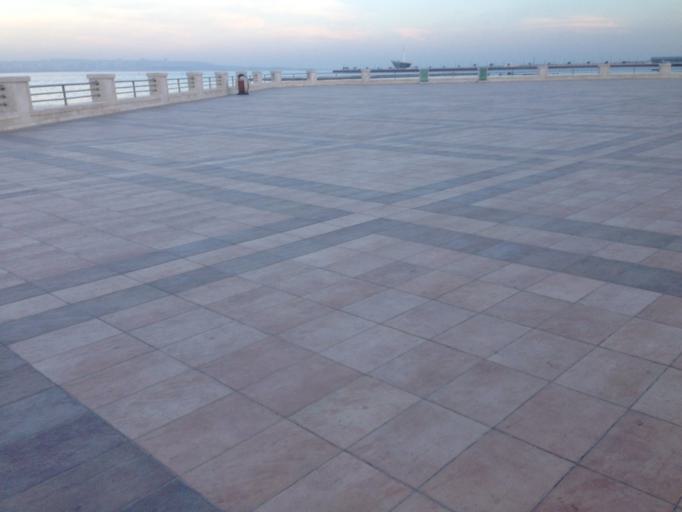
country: AZ
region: Baki
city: Badamdar
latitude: 40.3539
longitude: 49.8366
